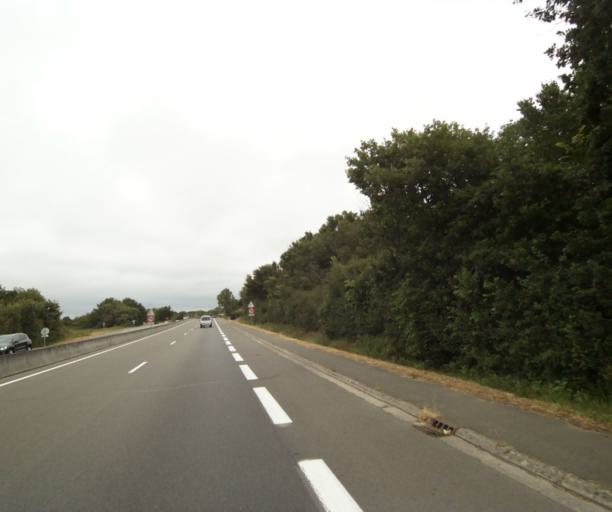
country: FR
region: Pays de la Loire
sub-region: Departement de la Vendee
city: Olonne-sur-Mer
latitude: 46.5156
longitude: -1.7648
